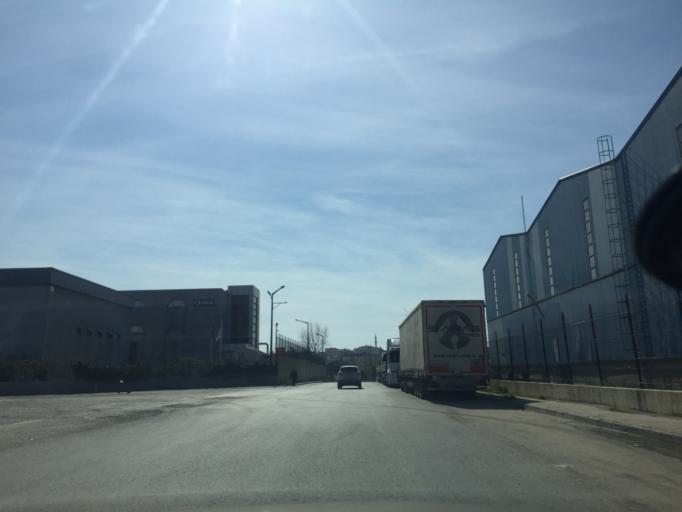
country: TR
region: Istanbul
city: Icmeler
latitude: 40.8380
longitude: 29.3159
